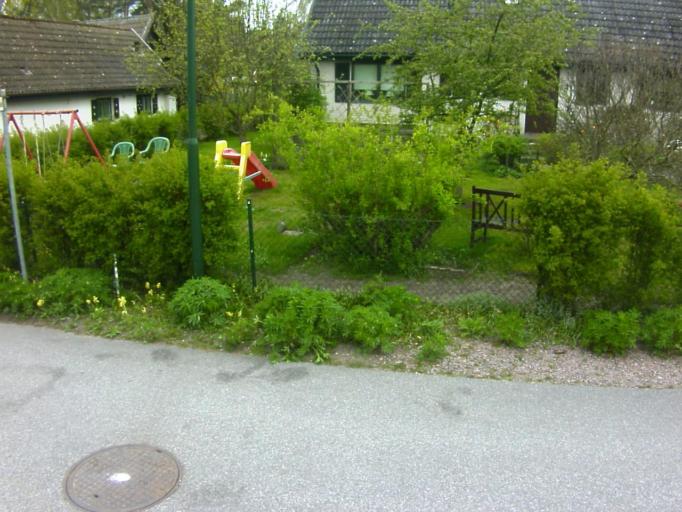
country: SE
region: Skane
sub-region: Kavlinge Kommun
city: Loddekopinge
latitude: 55.7536
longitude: 12.9954
